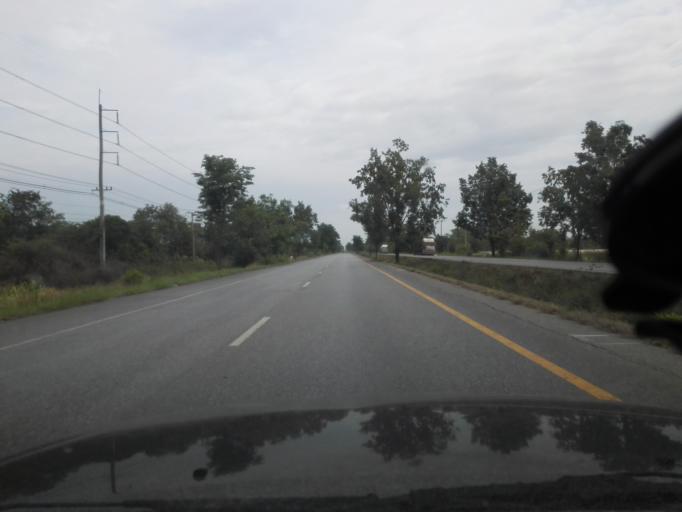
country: TH
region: Kamphaeng Phet
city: Khlong Khlung
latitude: 16.1174
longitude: 99.7194
